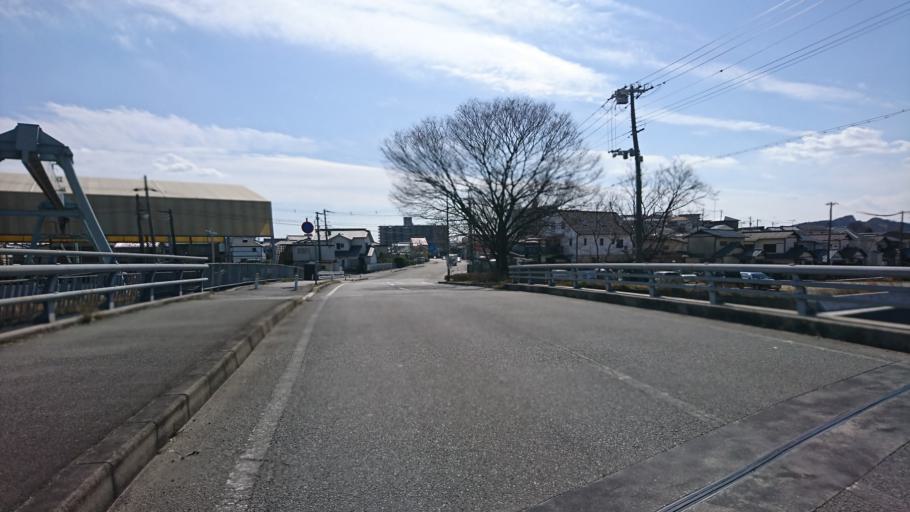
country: JP
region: Hyogo
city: Kakogawacho-honmachi
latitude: 34.7950
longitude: 134.8072
